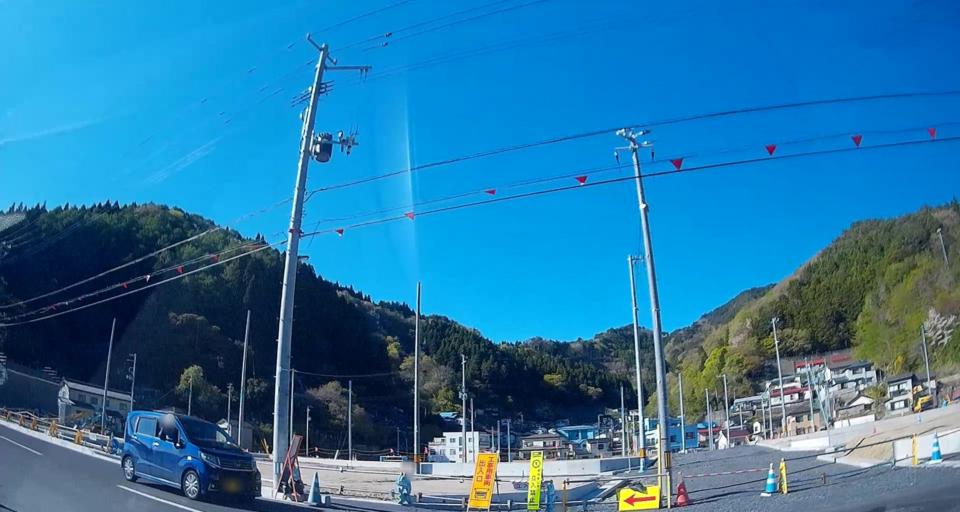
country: JP
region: Iwate
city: Kamaishi
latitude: 39.2754
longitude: 141.8912
